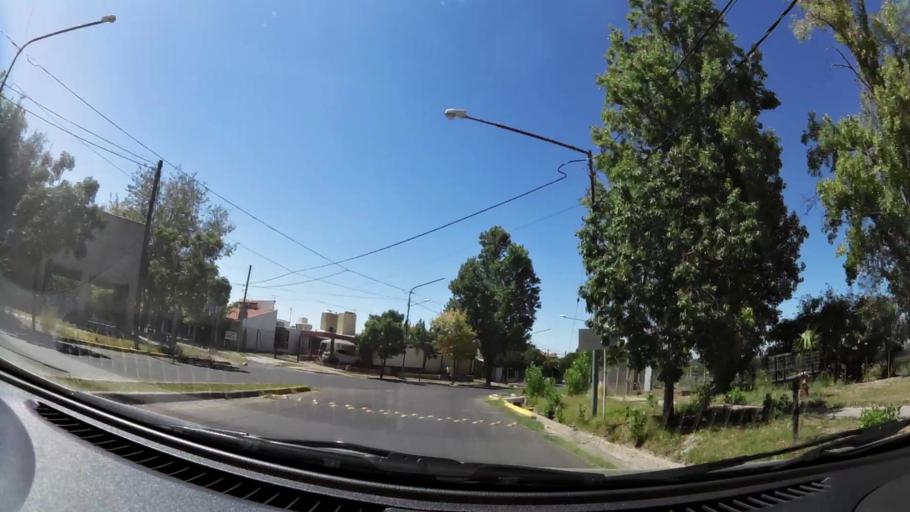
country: AR
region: Mendoza
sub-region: Departamento de Godoy Cruz
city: Godoy Cruz
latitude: -32.9512
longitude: -68.8595
